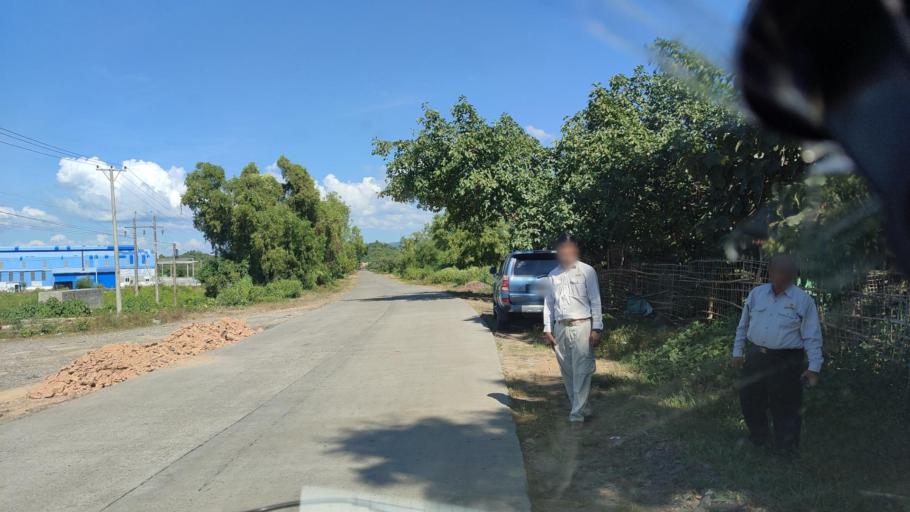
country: MM
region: Rakhine
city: Sittwe
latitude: 20.3901
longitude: 93.3246
